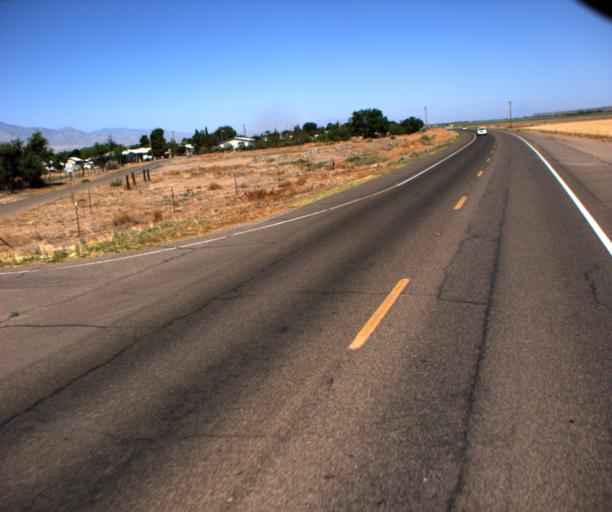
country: US
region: Arizona
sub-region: Graham County
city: Safford
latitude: 32.8150
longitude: -109.6244
